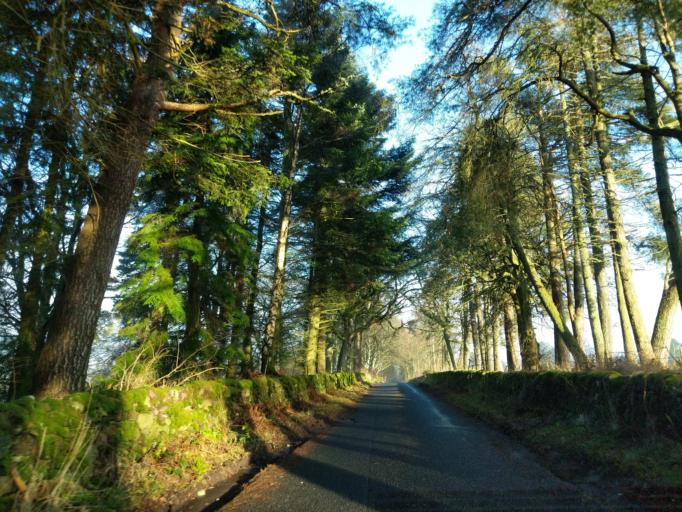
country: GB
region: Scotland
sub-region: Perth and Kinross
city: Auchterarder
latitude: 56.2647
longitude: -3.7190
